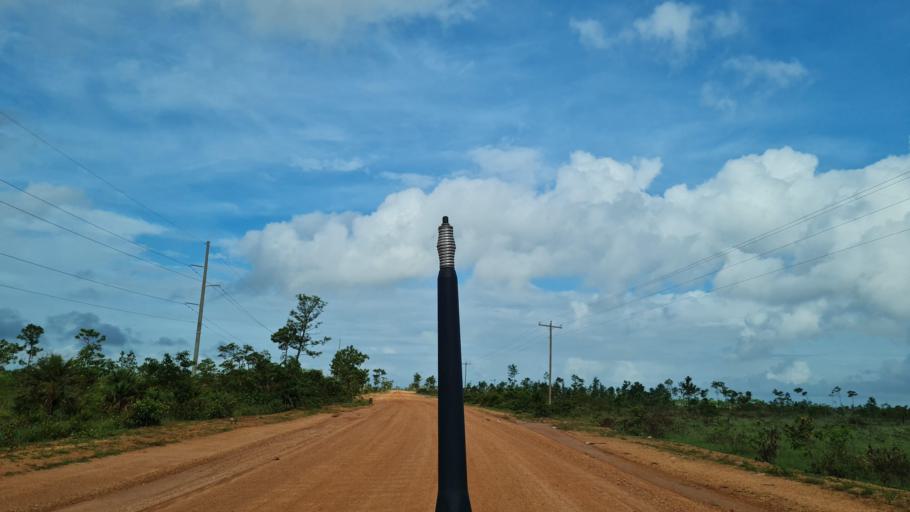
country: NI
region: Atlantico Norte (RAAN)
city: Puerto Cabezas
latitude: 14.1682
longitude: -83.4736
